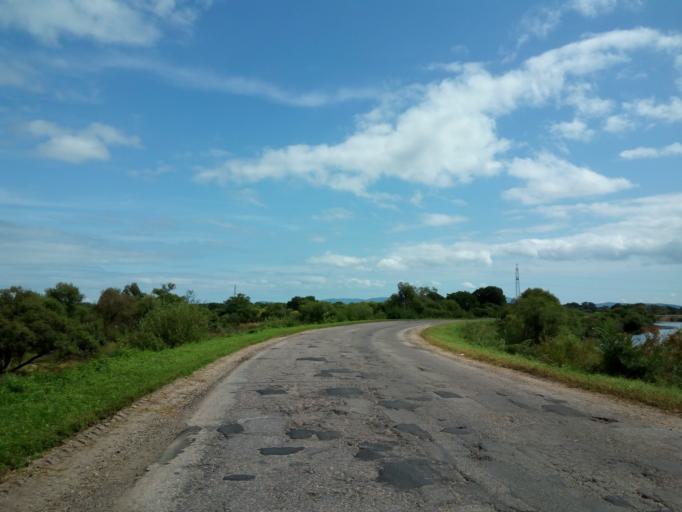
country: RU
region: Primorskiy
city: Dal'nerechensk
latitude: 45.9700
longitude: 133.7785
